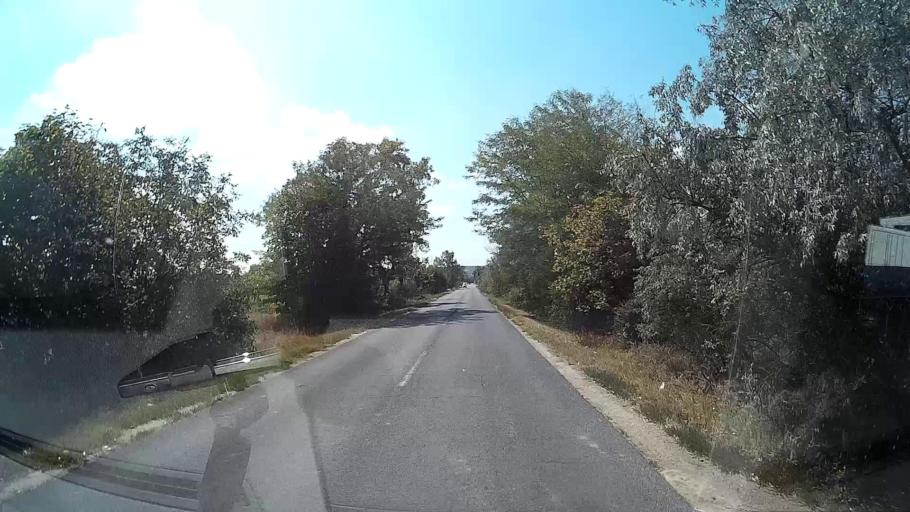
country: HU
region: Pest
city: Budakalasz
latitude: 47.6361
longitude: 19.0629
